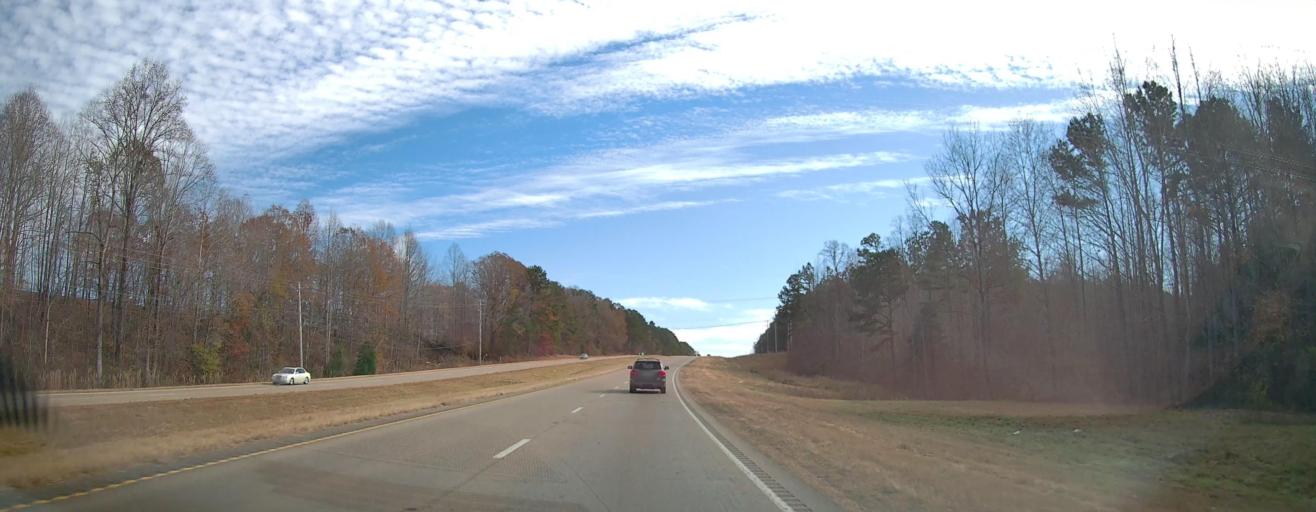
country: US
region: Mississippi
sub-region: Alcorn County
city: Farmington
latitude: 34.8894
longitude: -88.4595
